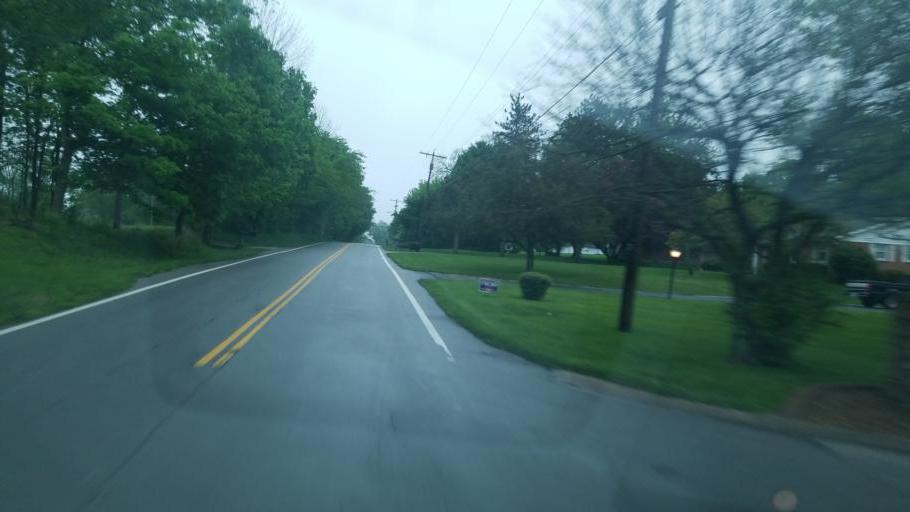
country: US
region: Ohio
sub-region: Highland County
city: Hillsboro
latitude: 39.1978
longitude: -83.6297
